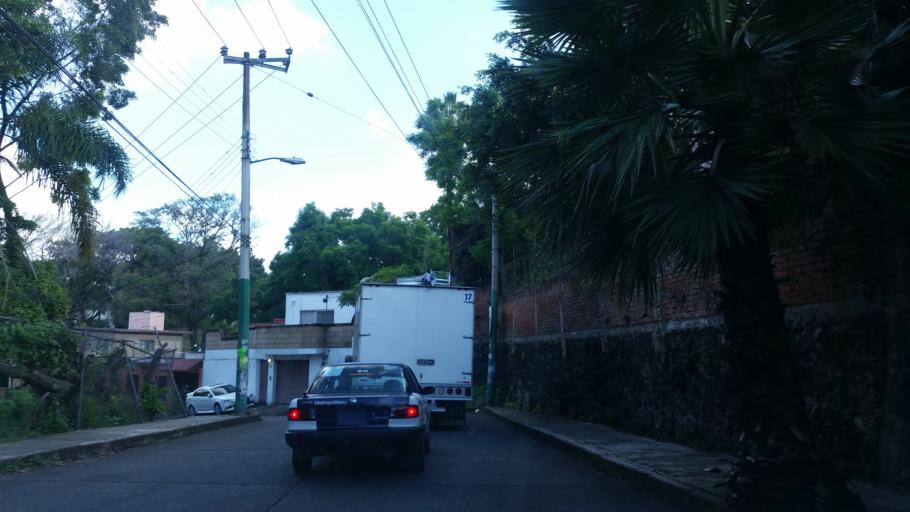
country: MX
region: Morelos
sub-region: Cuernavaca
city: Cuernavaca
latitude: 18.9197
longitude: -99.2084
